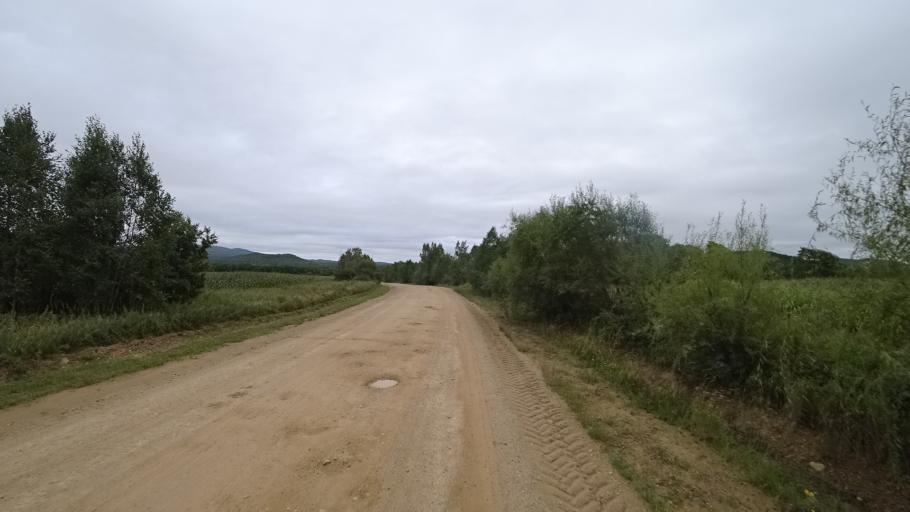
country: RU
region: Primorskiy
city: Rettikhovka
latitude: 44.1590
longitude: 132.7086
